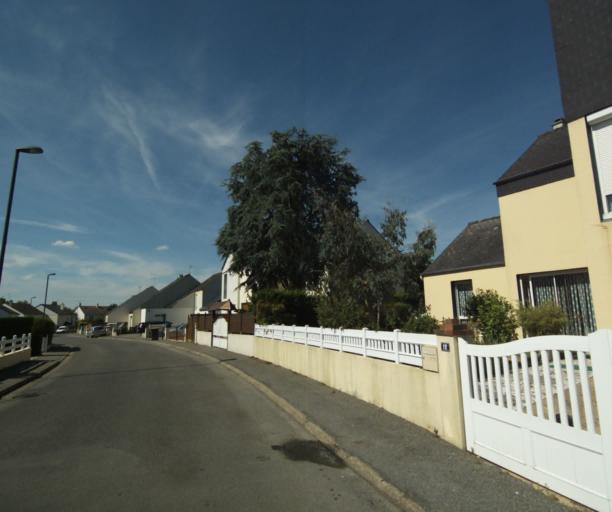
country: FR
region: Pays de la Loire
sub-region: Departement de la Mayenne
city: Laval
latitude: 48.0605
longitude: -0.7890
